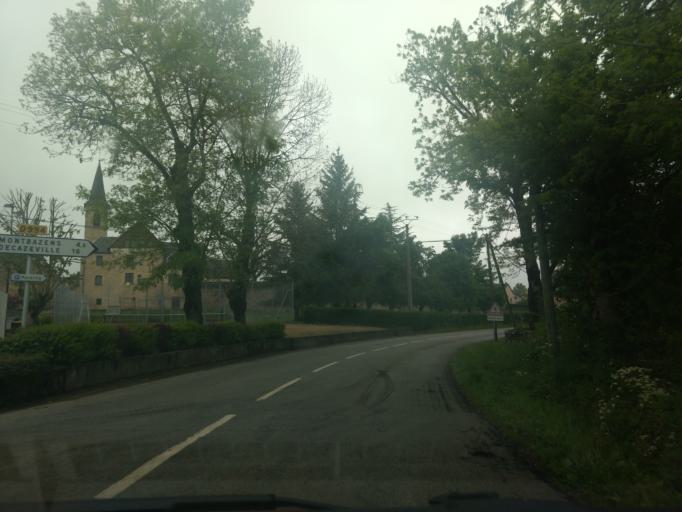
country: FR
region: Midi-Pyrenees
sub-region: Departement de l'Aveyron
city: Montbazens
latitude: 44.4523
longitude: 2.2526
